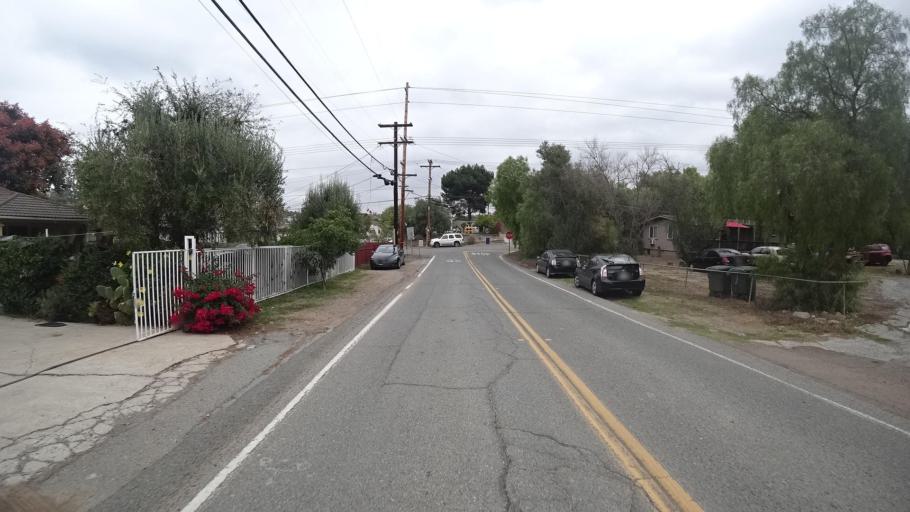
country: US
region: California
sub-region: San Diego County
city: Spring Valley
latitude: 32.7390
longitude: -117.0002
